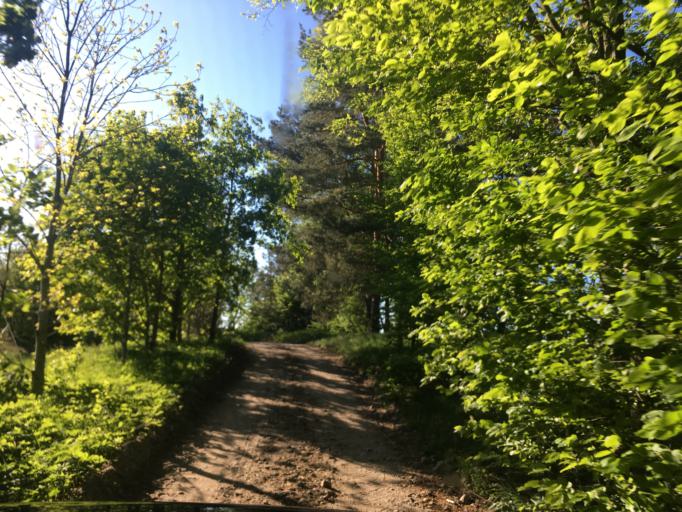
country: PL
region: Warmian-Masurian Voivodeship
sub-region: Powiat piski
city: Ruciane-Nida
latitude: 53.6568
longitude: 21.4831
